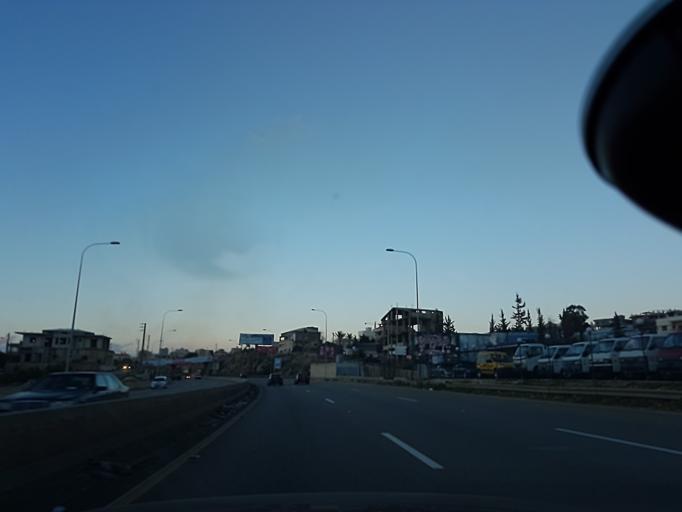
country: LB
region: Liban-Sud
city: Sidon
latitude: 33.6118
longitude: 35.4056
